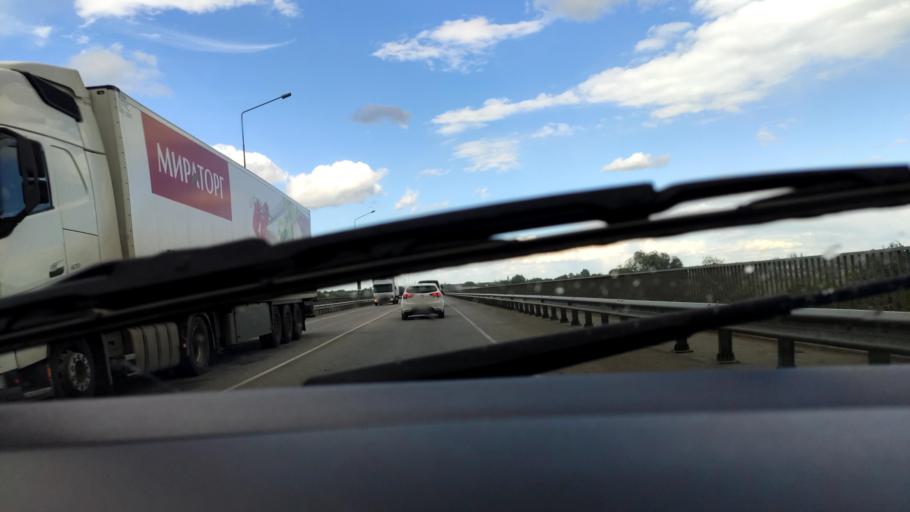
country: RU
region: Voronezj
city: Somovo
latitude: 51.6825
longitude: 39.3472
